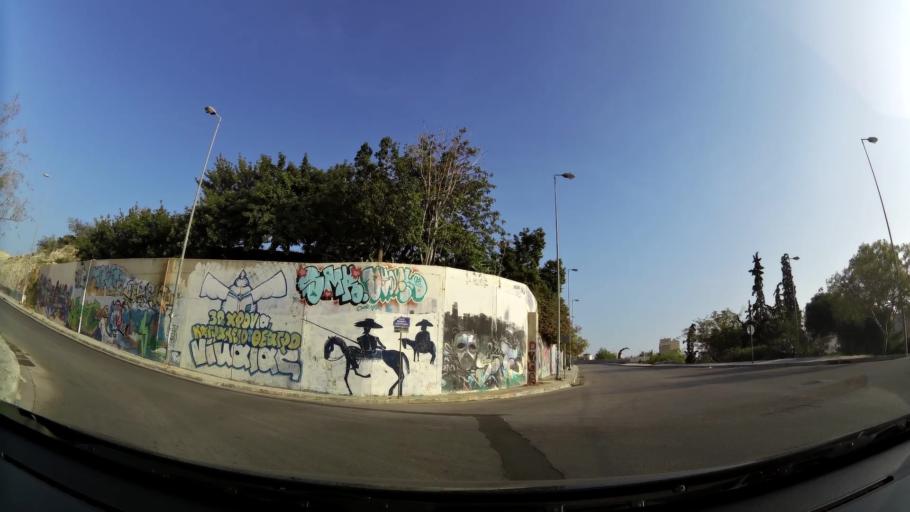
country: GR
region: Attica
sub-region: Nomos Piraios
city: Keratsini
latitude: 37.9684
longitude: 23.6343
